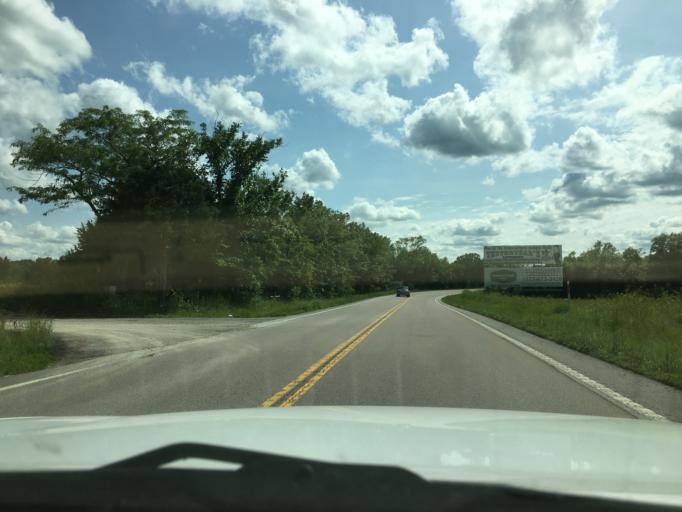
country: US
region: Missouri
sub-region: Franklin County
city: Gerald
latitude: 38.3908
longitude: -91.3705
